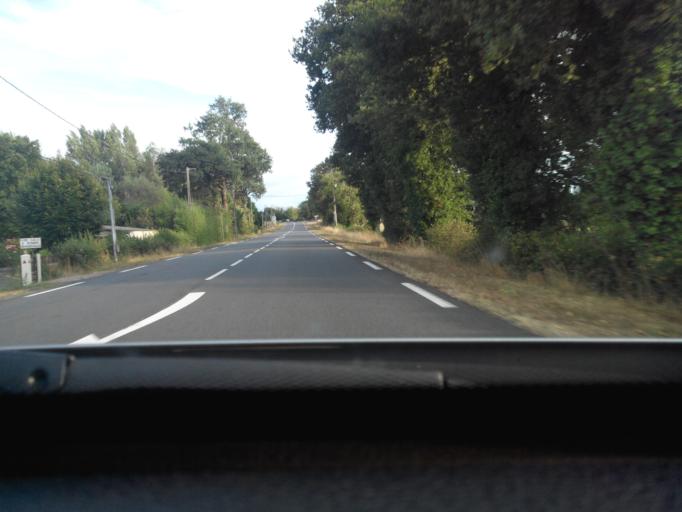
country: FR
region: Poitou-Charentes
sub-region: Departement de la Charente
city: Etagnac
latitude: 45.9172
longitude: 0.7457
